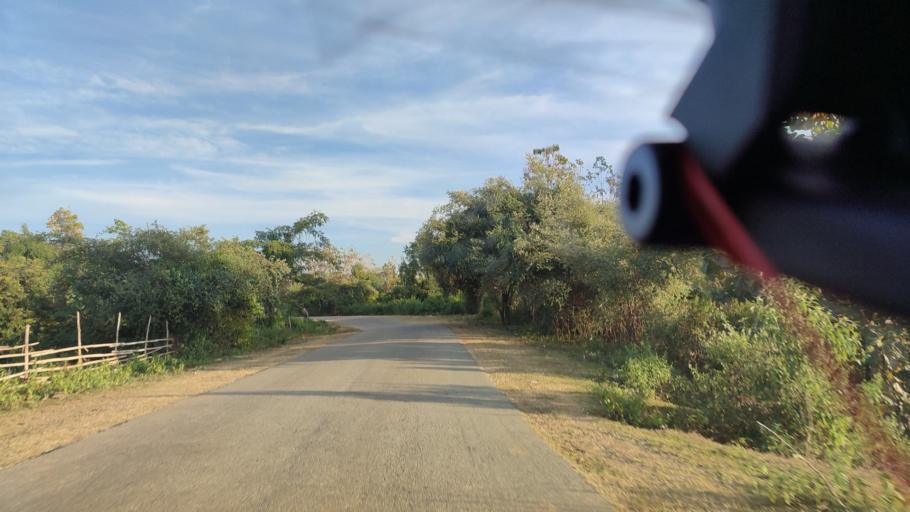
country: MM
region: Mandalay
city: Nay Pyi Taw
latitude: 19.9976
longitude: 95.9226
